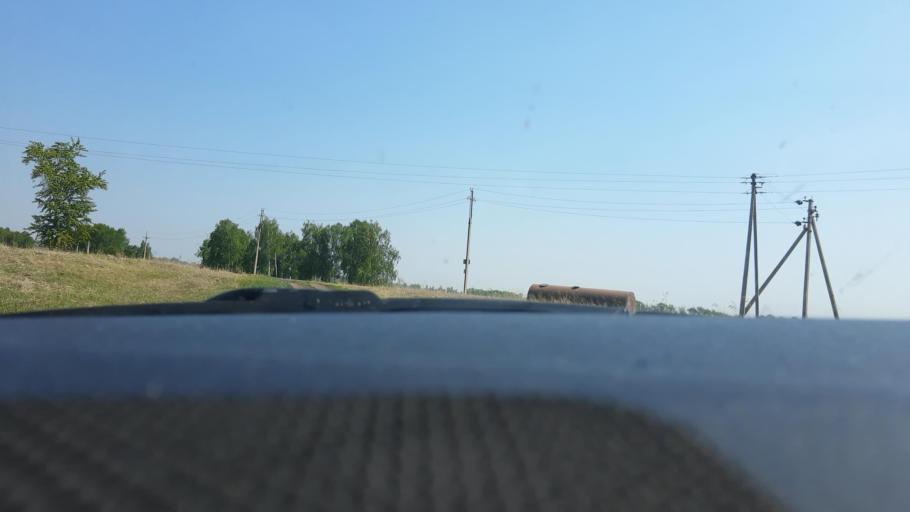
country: RU
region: Bashkortostan
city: Chishmy
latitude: 54.4315
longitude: 55.2921
